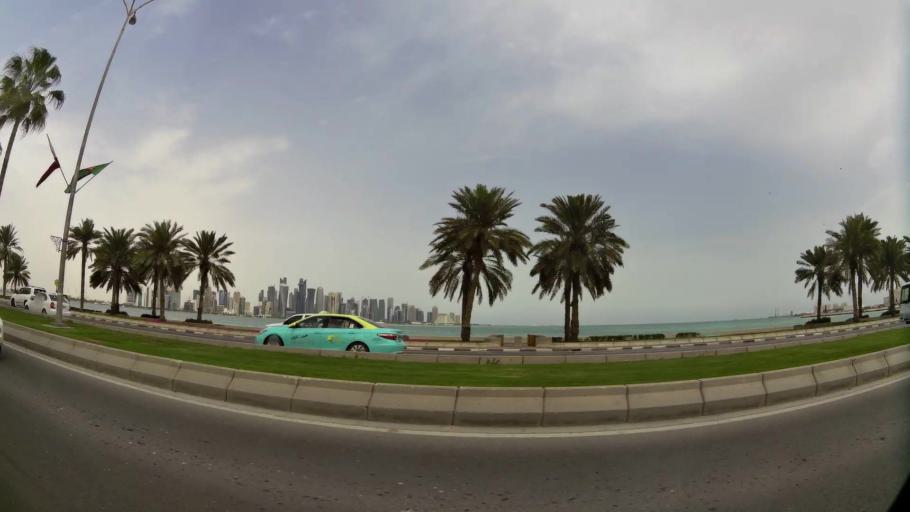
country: QA
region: Baladiyat ad Dawhah
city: Doha
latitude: 25.2935
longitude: 51.5264
